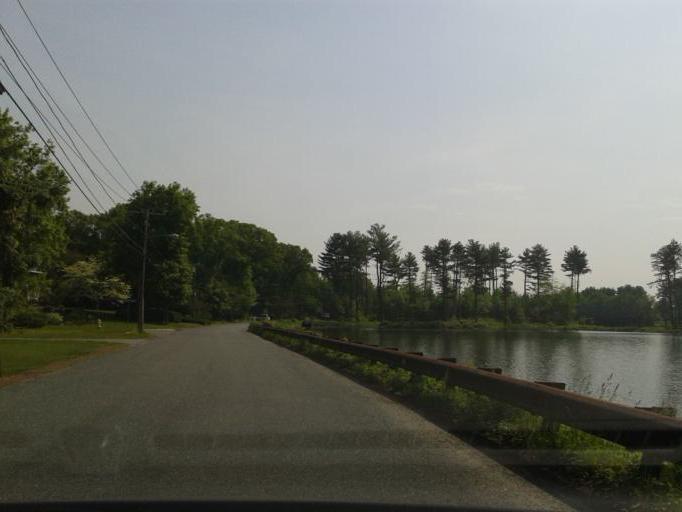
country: US
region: Massachusetts
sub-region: Worcester County
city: Westborough
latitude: 42.2430
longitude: -71.6083
